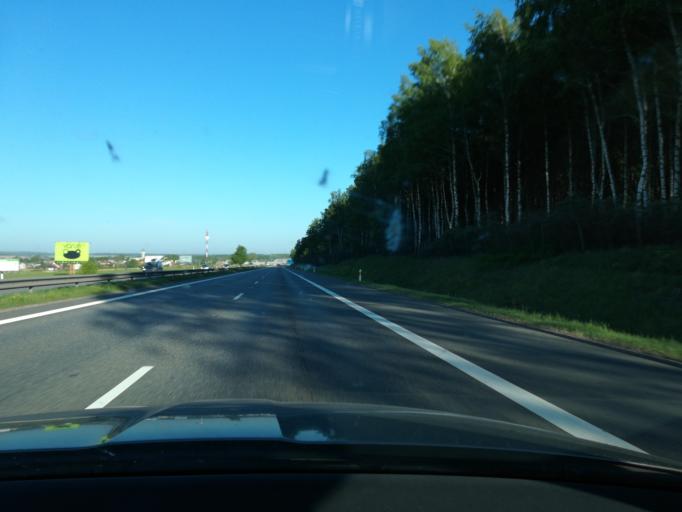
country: LT
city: Ziezmariai
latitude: 54.8091
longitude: 24.4695
